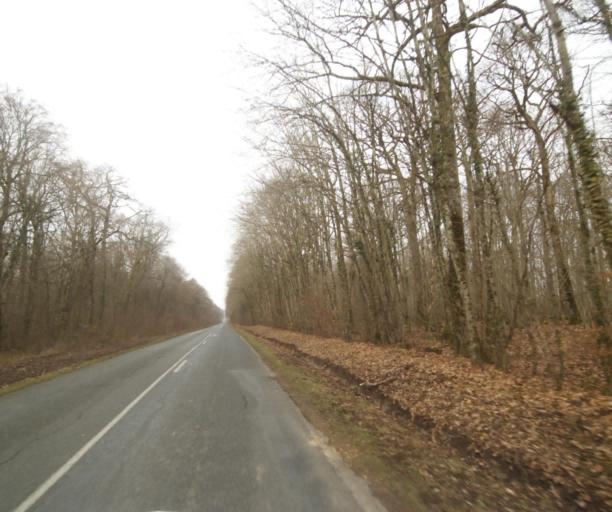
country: FR
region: Champagne-Ardenne
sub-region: Departement de la Haute-Marne
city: Villiers-en-Lieu
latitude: 48.7101
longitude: 4.8886
